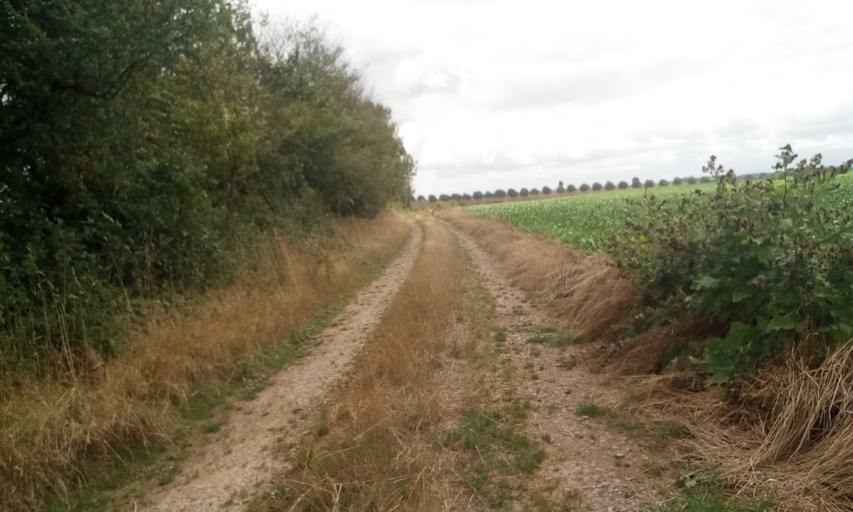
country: FR
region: Lower Normandy
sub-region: Departement du Calvados
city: Cheux
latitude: 49.1821
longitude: -0.5437
